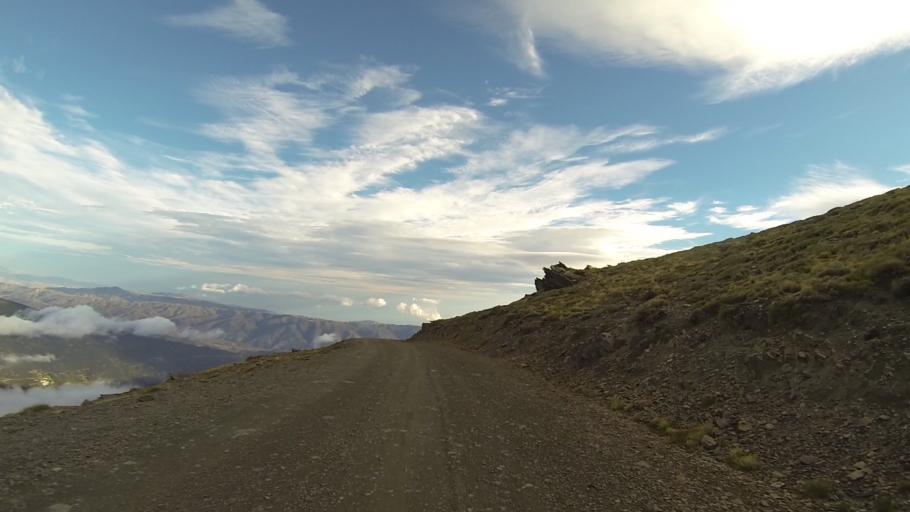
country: ES
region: Andalusia
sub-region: Provincia de Granada
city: Trevelez
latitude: 36.9915
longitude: -3.3115
